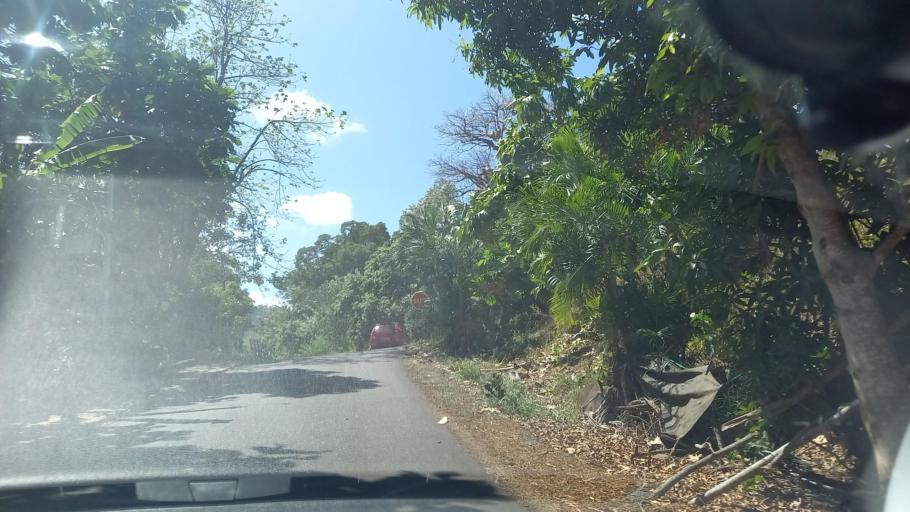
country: YT
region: Kani-Keli
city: Kani Keli
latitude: -12.9615
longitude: 45.1119
